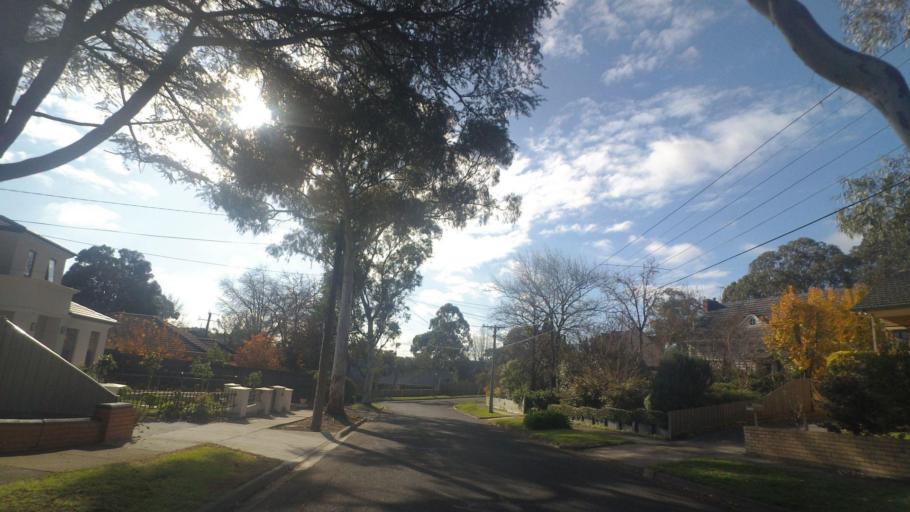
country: AU
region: Victoria
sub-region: Whitehorse
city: Mont Albert North
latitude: -37.7993
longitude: 145.1079
